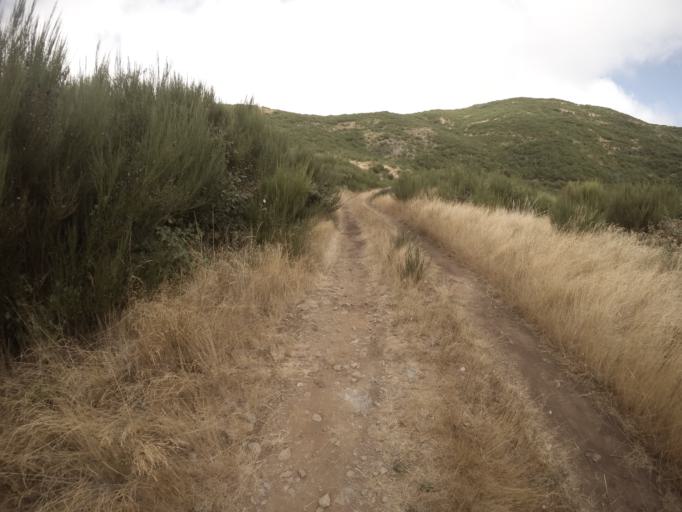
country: PT
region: Madeira
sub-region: Camara de Lobos
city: Curral das Freiras
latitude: 32.7124
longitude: -16.9963
